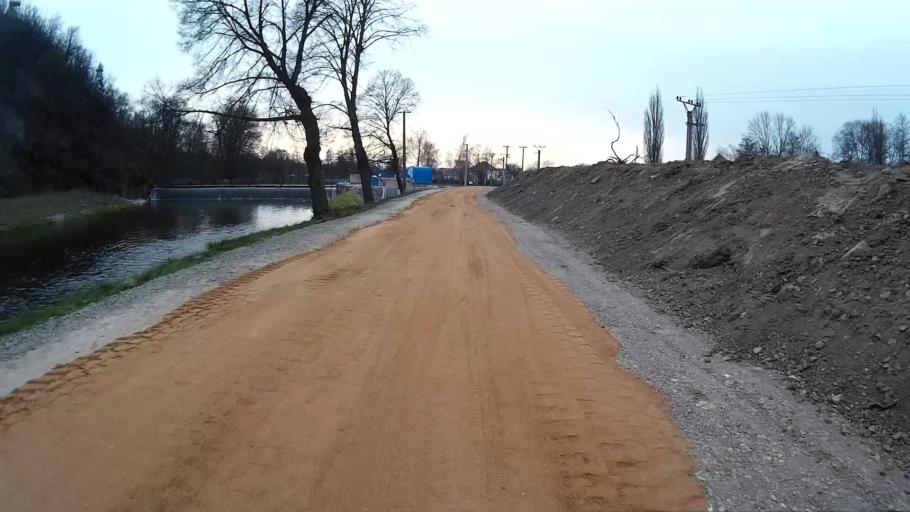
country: CZ
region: South Moravian
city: Ivancice
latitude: 49.0984
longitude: 16.3867
